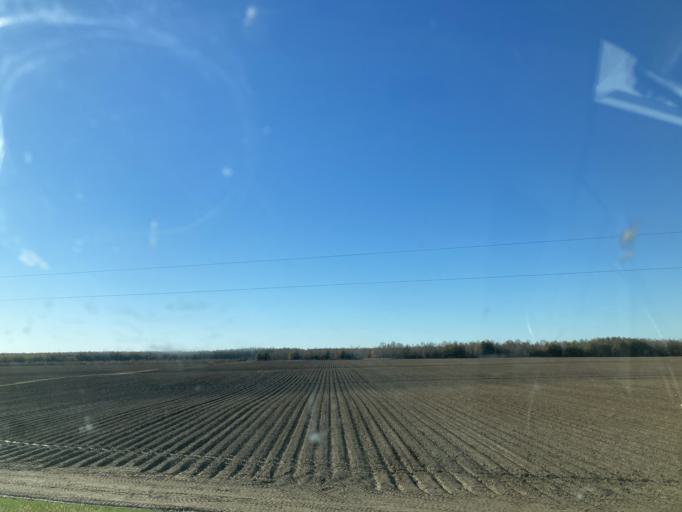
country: US
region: Mississippi
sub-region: Yazoo County
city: Yazoo City
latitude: 32.7789
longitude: -90.6368
